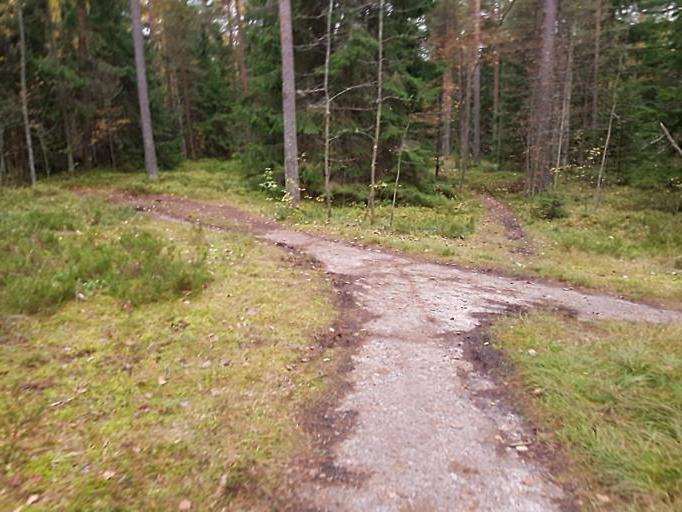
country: FI
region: Uusimaa
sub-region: Helsinki
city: Helsinki
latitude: 60.2580
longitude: 24.9016
